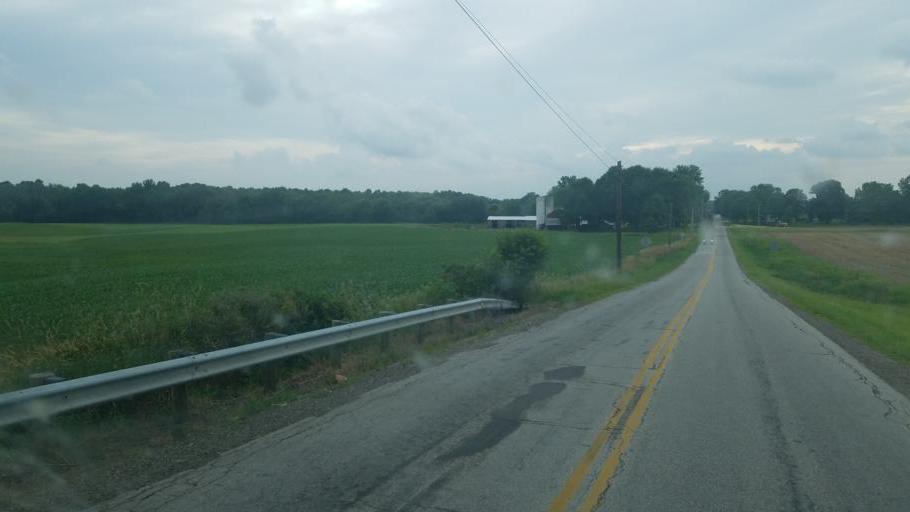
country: US
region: Ohio
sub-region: Wayne County
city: Orrville
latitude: 40.8220
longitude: -81.7655
